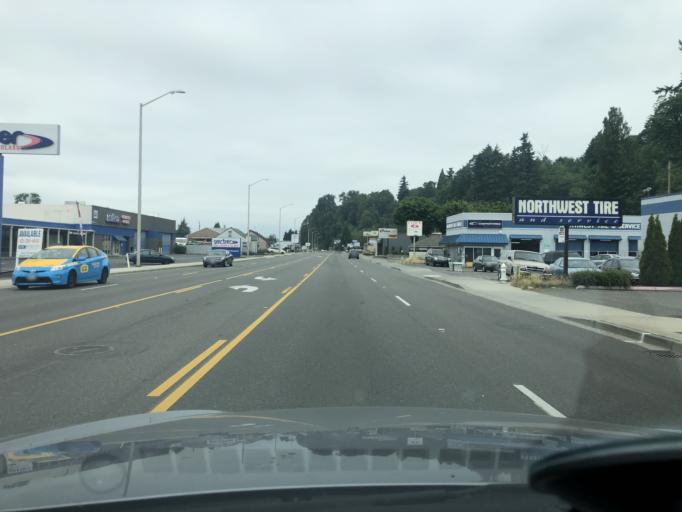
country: US
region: Washington
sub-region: King County
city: Kent
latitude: 47.3730
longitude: -122.2303
